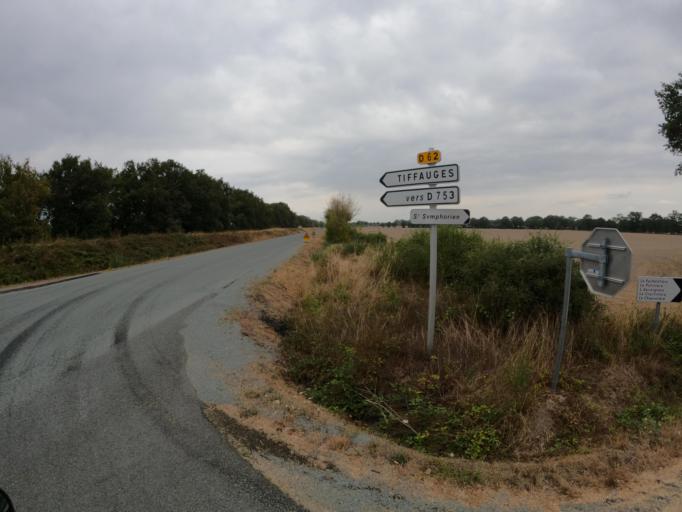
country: FR
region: Pays de la Loire
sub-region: Departement de la Vendee
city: Treize-Septiers
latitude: 46.9782
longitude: -1.2047
